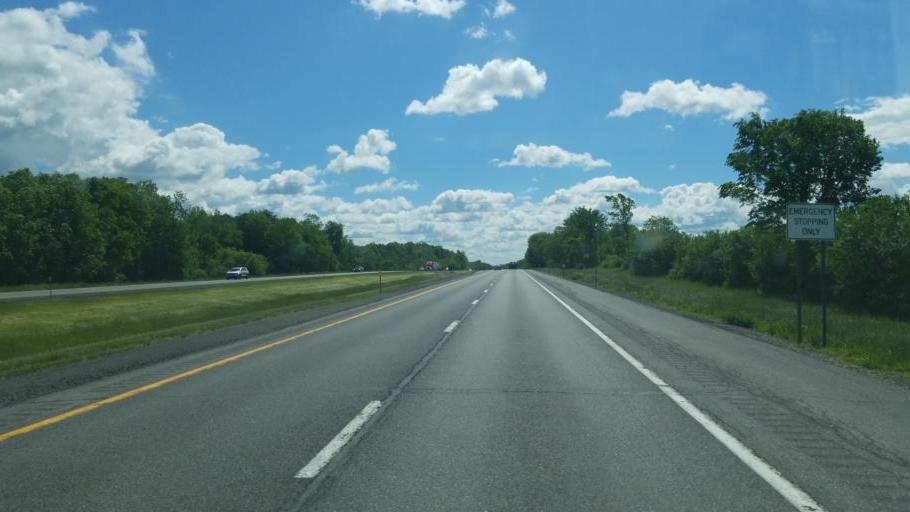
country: US
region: New York
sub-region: Oneida County
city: Rome
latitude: 43.1344
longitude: -75.4729
